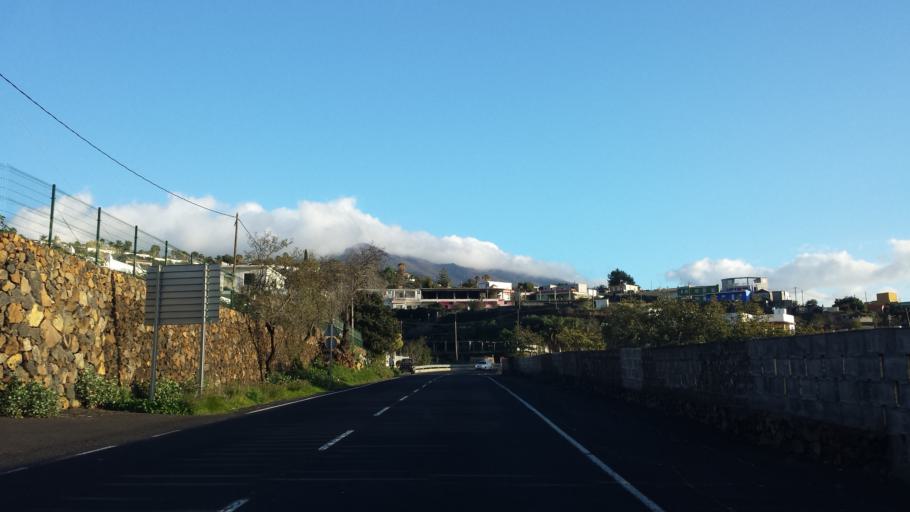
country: ES
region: Canary Islands
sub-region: Provincia de Santa Cruz de Tenerife
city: Los Llanos de Aridane
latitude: 28.6517
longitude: -17.9012
